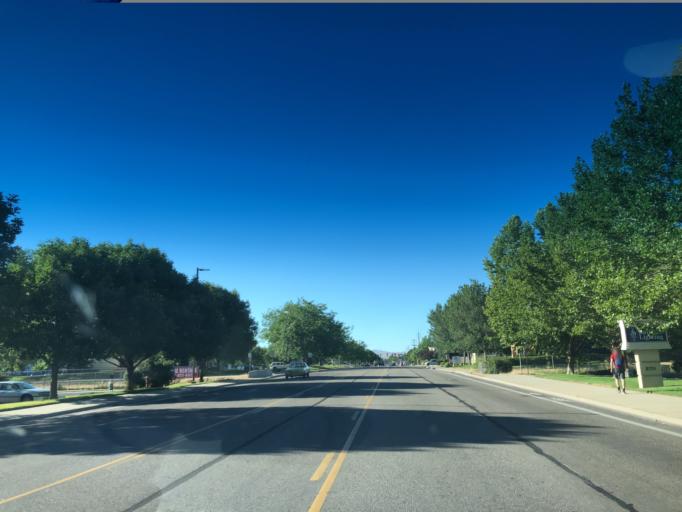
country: US
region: Idaho
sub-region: Ada County
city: Garden City
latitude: 43.6127
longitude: -116.2841
